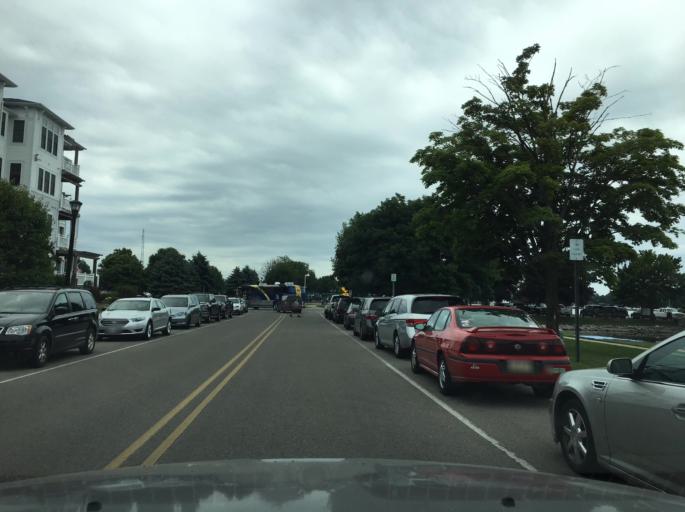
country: US
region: Michigan
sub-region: Mason County
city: Ludington
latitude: 43.9542
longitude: -86.4521
